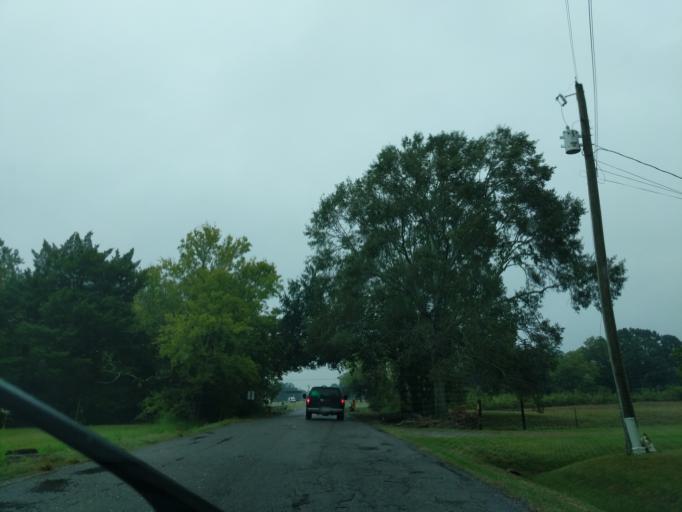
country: US
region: Louisiana
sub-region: Vermilion Parish
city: Kaplan
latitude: 29.9927
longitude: -92.2828
